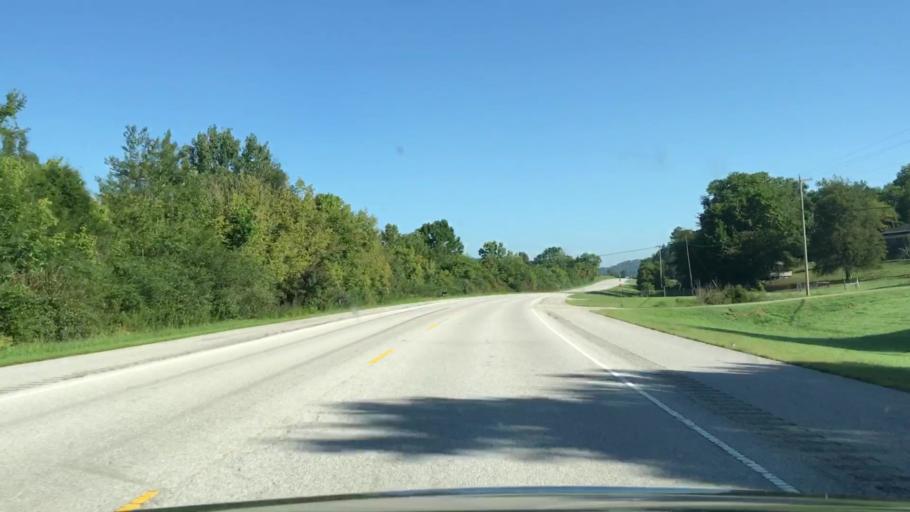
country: US
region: Tennessee
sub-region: Jackson County
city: Gainesboro
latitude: 36.4088
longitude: -85.6377
